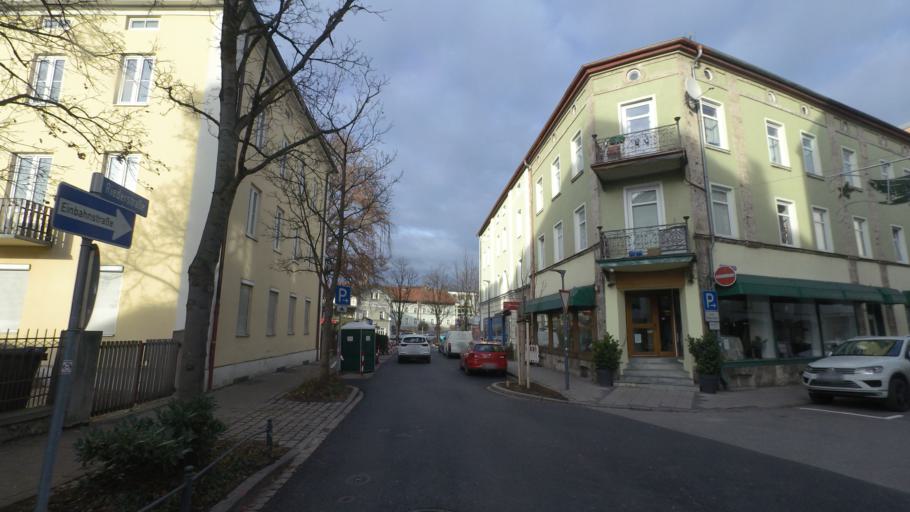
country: DE
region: Bavaria
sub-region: Upper Bavaria
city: Rosenheim
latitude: 47.8539
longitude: 12.1224
